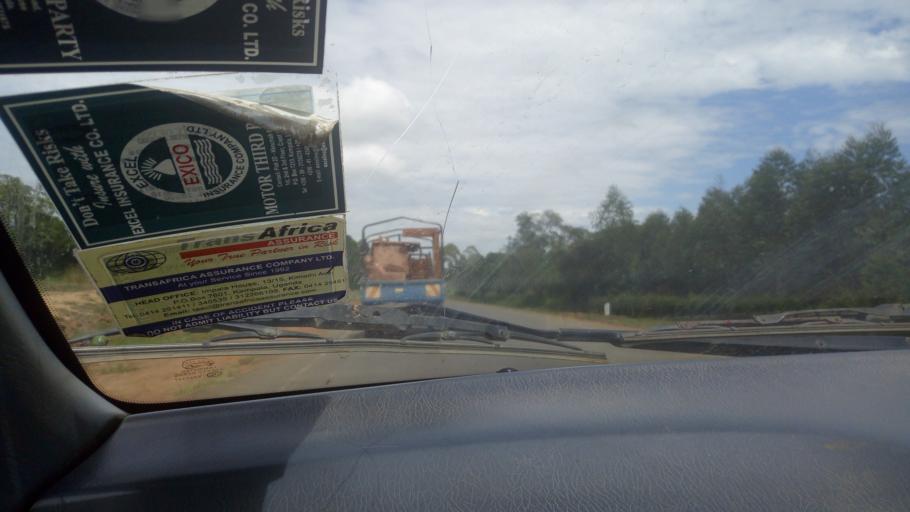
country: UG
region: Western Region
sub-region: Mbarara District
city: Bwizibwera
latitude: -0.4211
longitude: 30.5704
